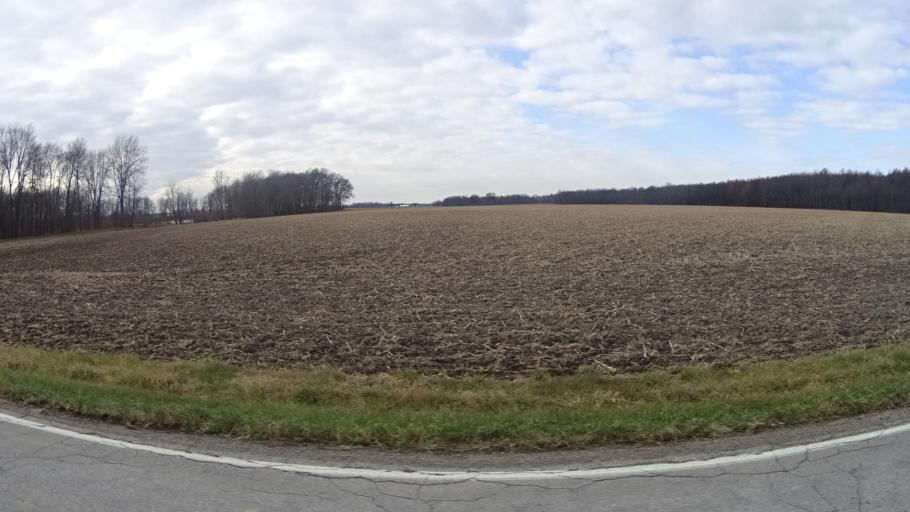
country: US
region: Ohio
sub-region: Lorain County
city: Camden
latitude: 41.2445
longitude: -82.3318
